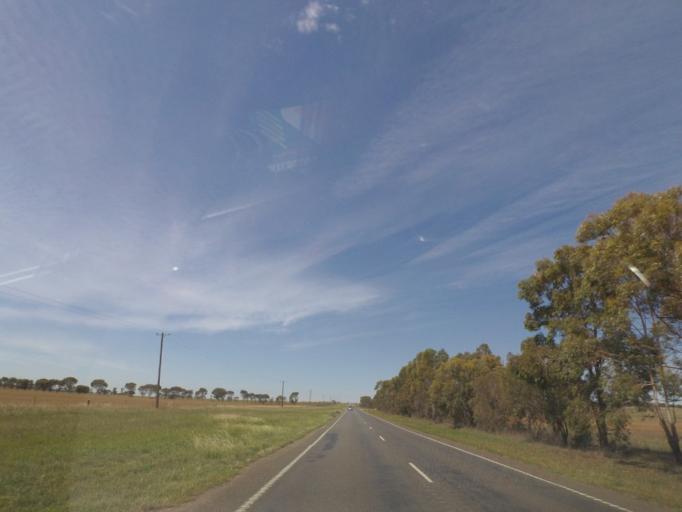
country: AU
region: Victoria
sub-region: Moorabool
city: Bacchus Marsh
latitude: -37.7647
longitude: 144.4402
